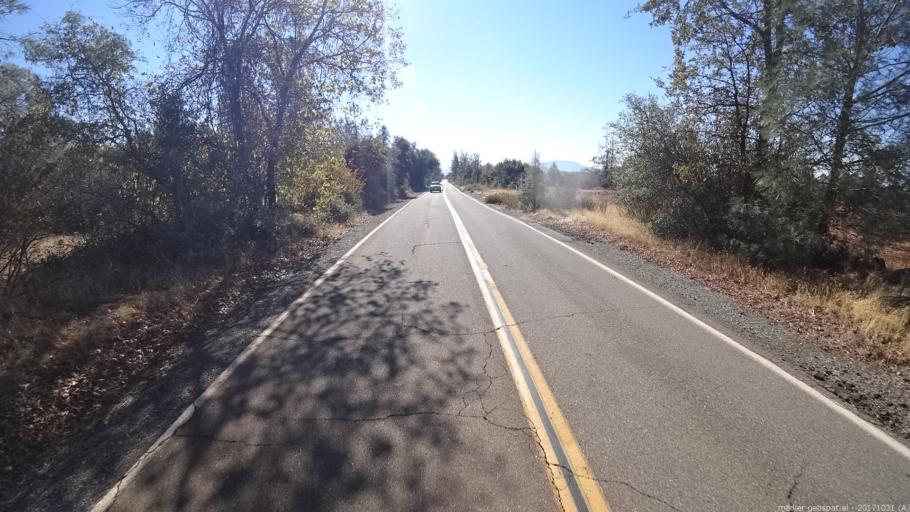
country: US
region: California
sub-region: Shasta County
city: Shingletown
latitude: 40.4512
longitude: -121.8994
